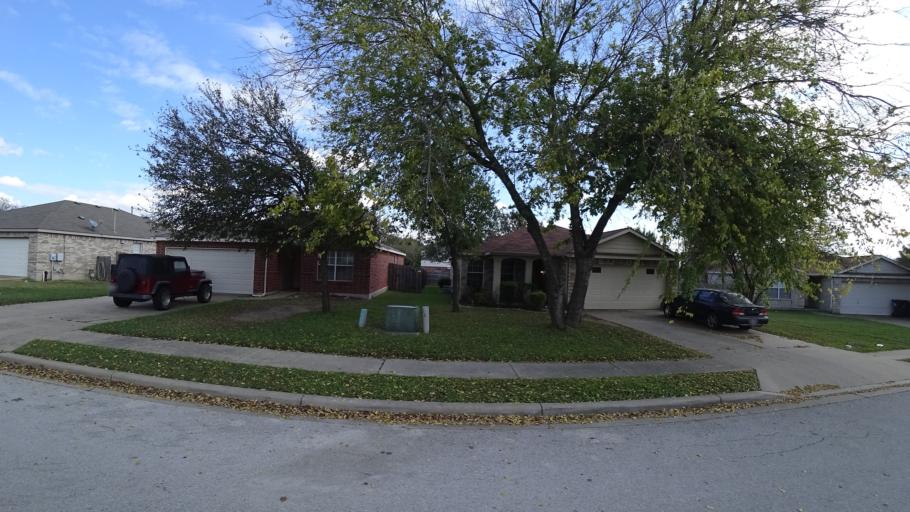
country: US
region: Texas
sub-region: Travis County
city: Pflugerville
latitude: 30.4340
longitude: -97.6355
